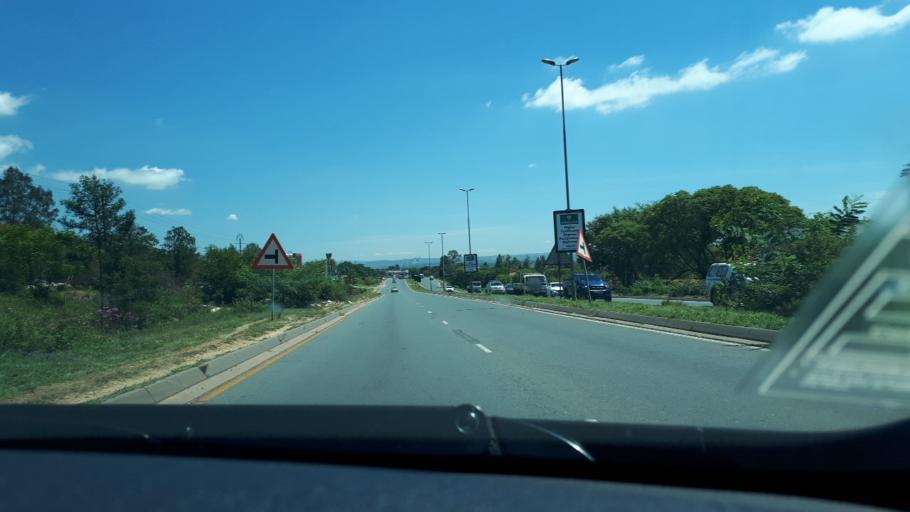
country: ZA
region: Gauteng
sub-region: West Rand District Municipality
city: Muldersdriseloop
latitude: -26.0579
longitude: 27.9548
